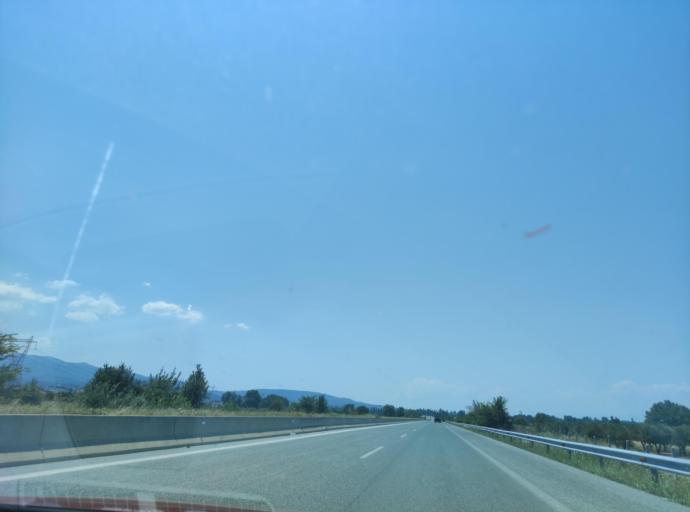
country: GR
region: Central Macedonia
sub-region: Nomos Serron
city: Charopo
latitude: 41.2608
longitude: 23.3533
